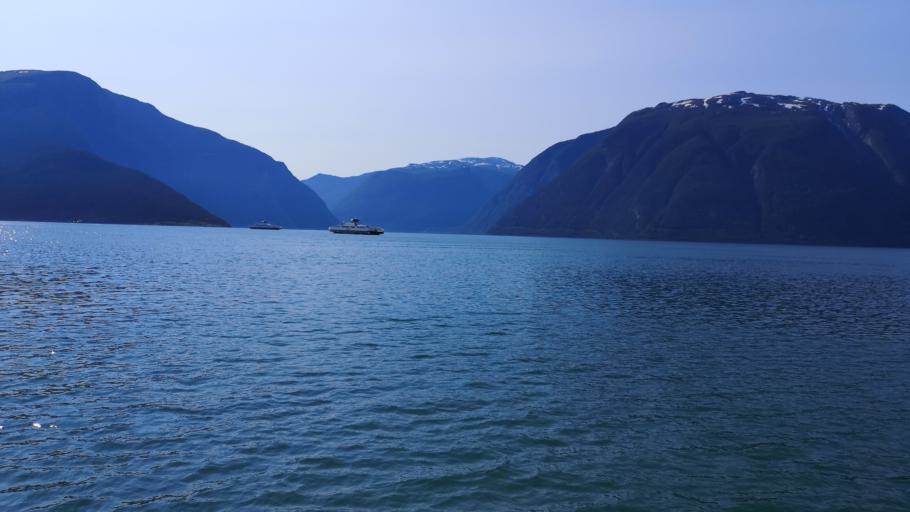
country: NO
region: Sogn og Fjordane
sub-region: Laerdal
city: Laerdalsoyri
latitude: 61.1603
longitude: 7.3375
